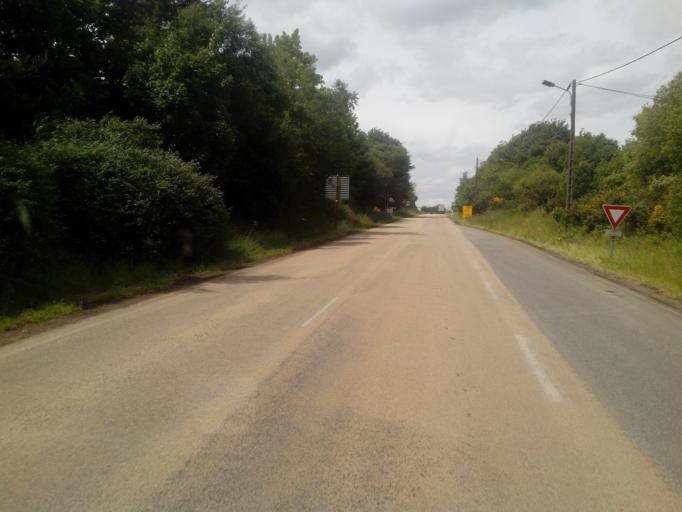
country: FR
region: Brittany
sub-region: Departement du Finistere
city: Guerlesquin
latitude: 48.5209
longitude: -3.5908
